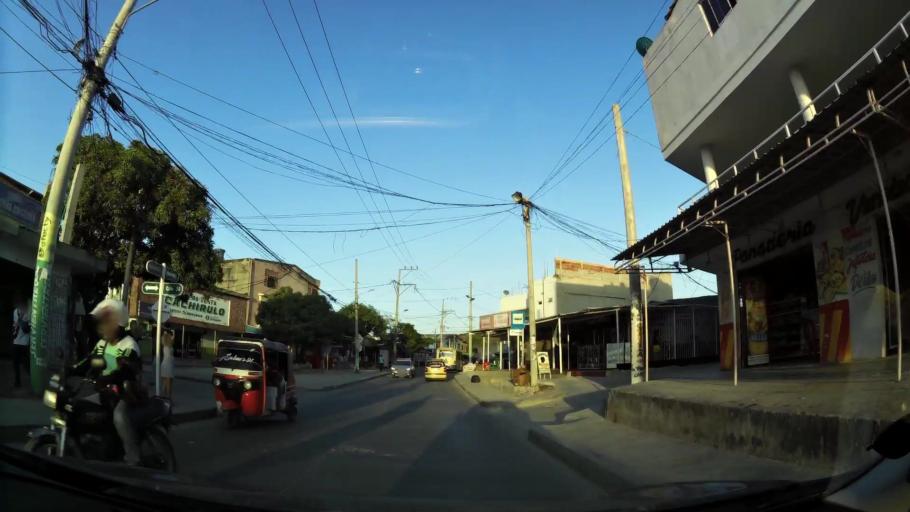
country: CO
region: Atlantico
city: Soledad
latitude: 10.9213
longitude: -74.7913
